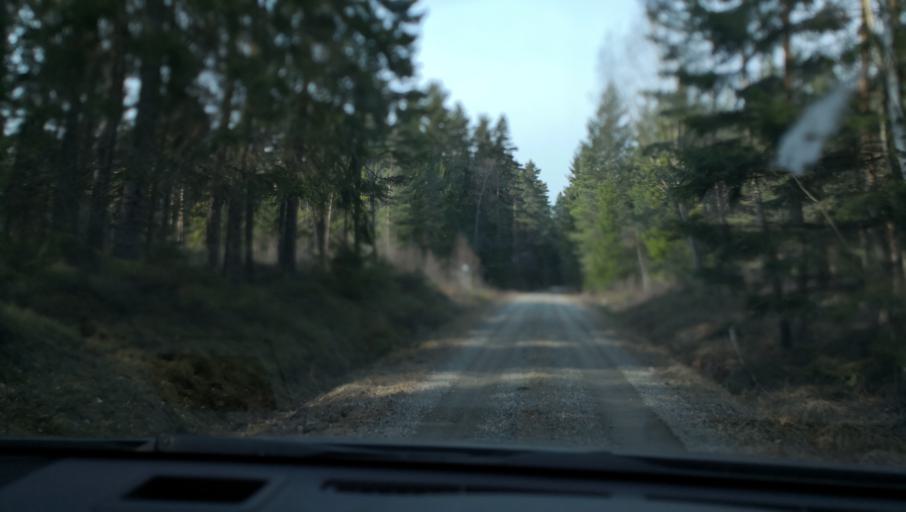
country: SE
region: OErebro
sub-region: Lindesbergs Kommun
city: Frovi
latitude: 59.3768
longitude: 15.4209
